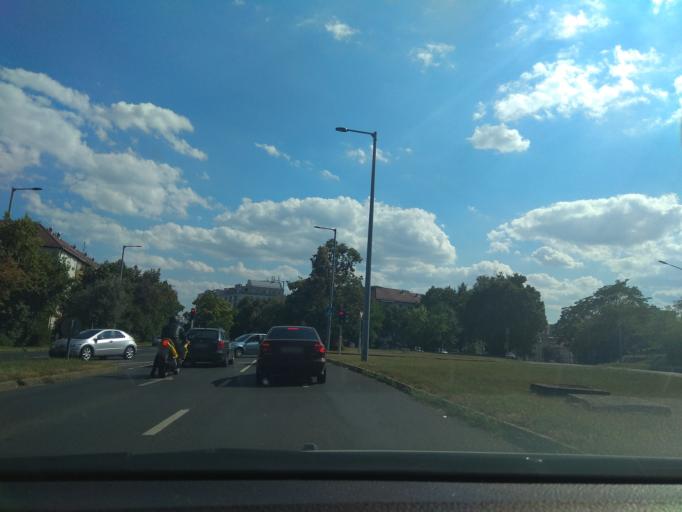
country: HU
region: Borsod-Abauj-Zemplen
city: Miskolc
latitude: 48.1098
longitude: 20.7881
